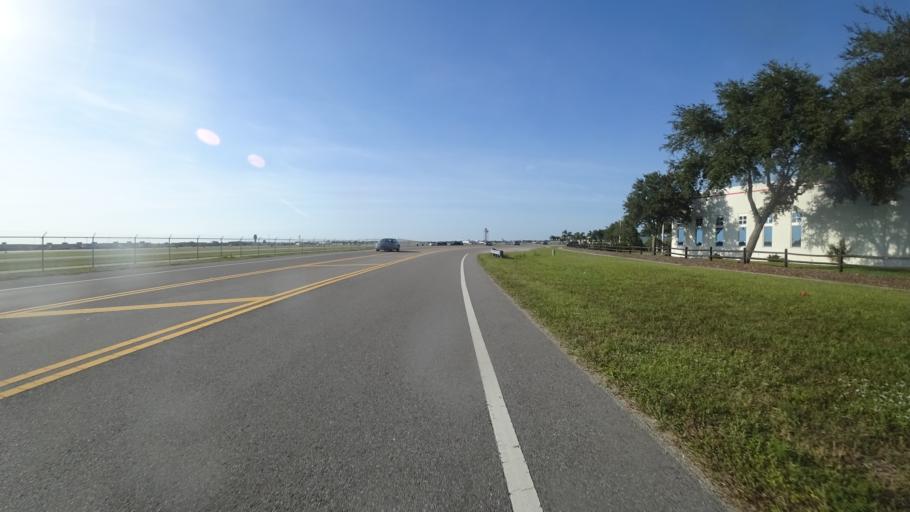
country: US
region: Florida
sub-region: Manatee County
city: Whitfield
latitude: 27.3898
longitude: -82.5455
